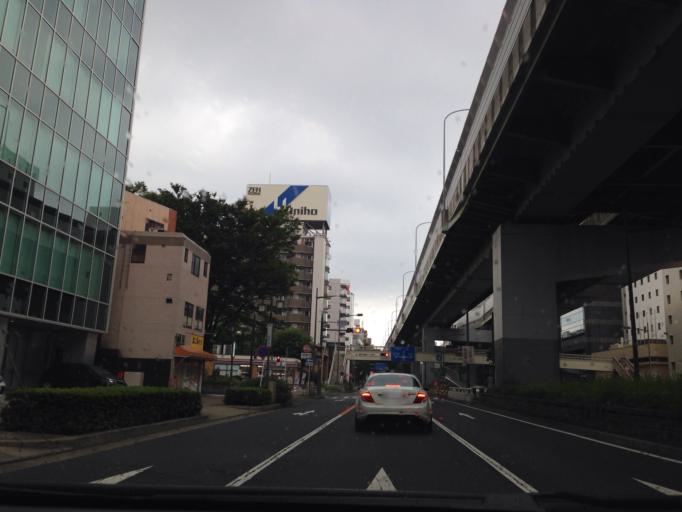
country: JP
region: Aichi
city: Nagoya-shi
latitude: 35.1717
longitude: 136.9142
